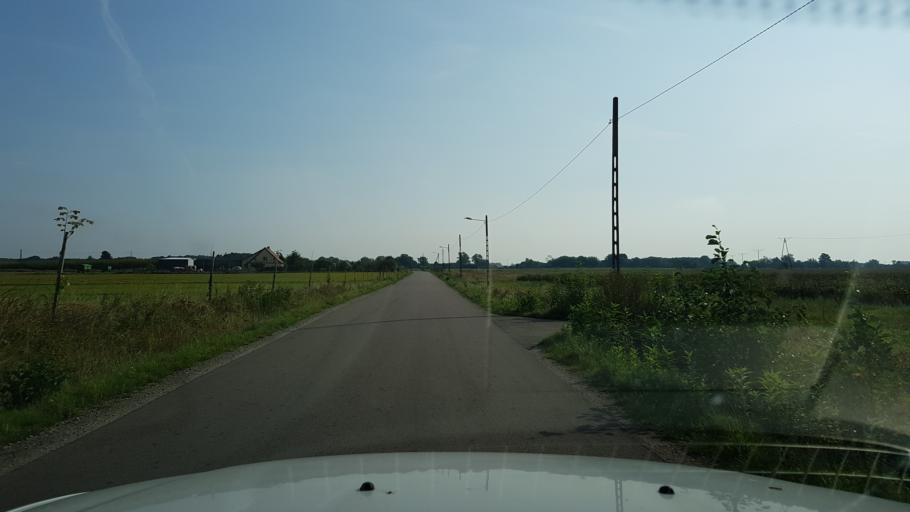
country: PL
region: West Pomeranian Voivodeship
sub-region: Powiat slawienski
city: Slawno
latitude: 54.3667
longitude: 16.5641
